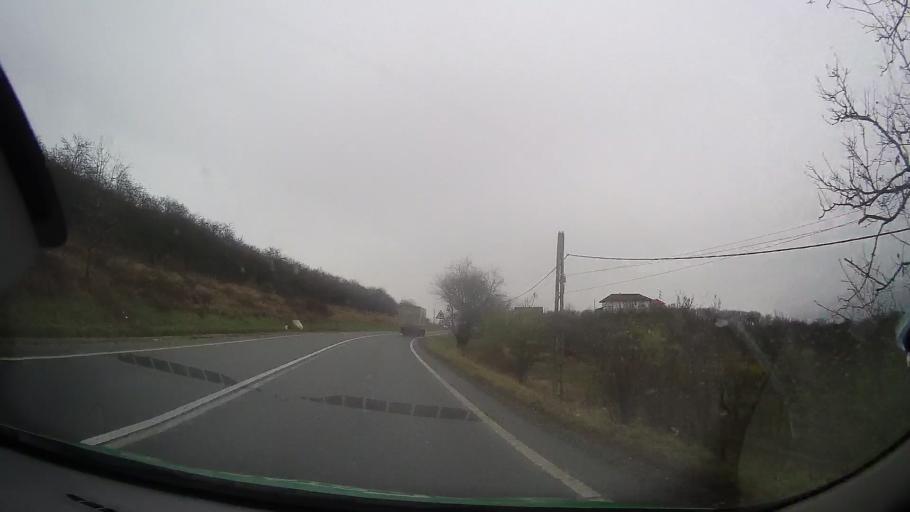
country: RO
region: Mures
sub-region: Comuna Breaza
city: Breaza
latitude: 46.7658
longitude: 24.6592
